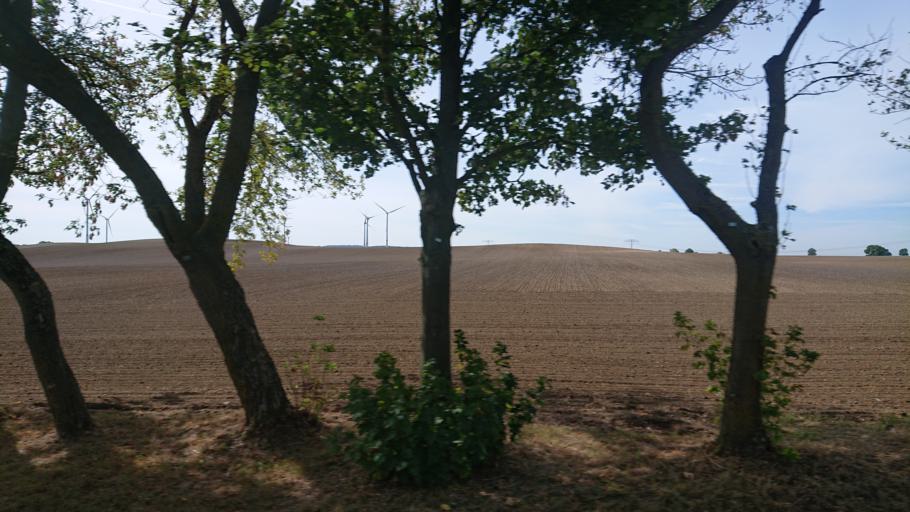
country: DE
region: Brandenburg
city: Gramzow
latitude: 53.2441
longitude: 13.9699
